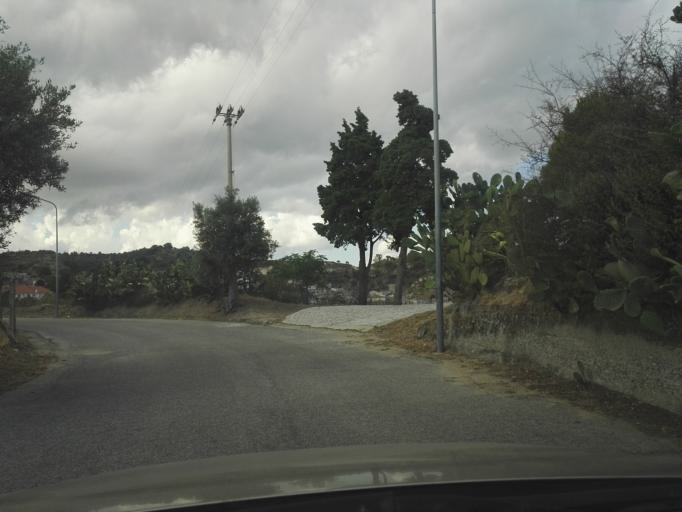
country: IT
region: Calabria
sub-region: Provincia di Reggio Calabria
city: Riace
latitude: 38.4148
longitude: 16.4829
